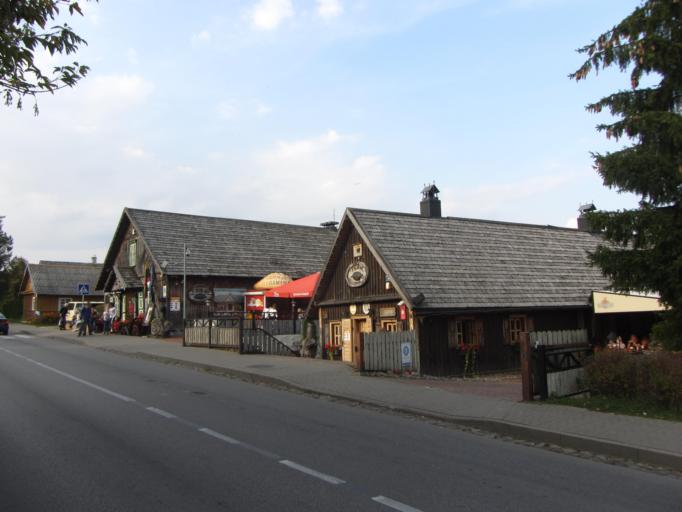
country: LT
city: Trakai
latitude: 54.6506
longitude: 24.9245
